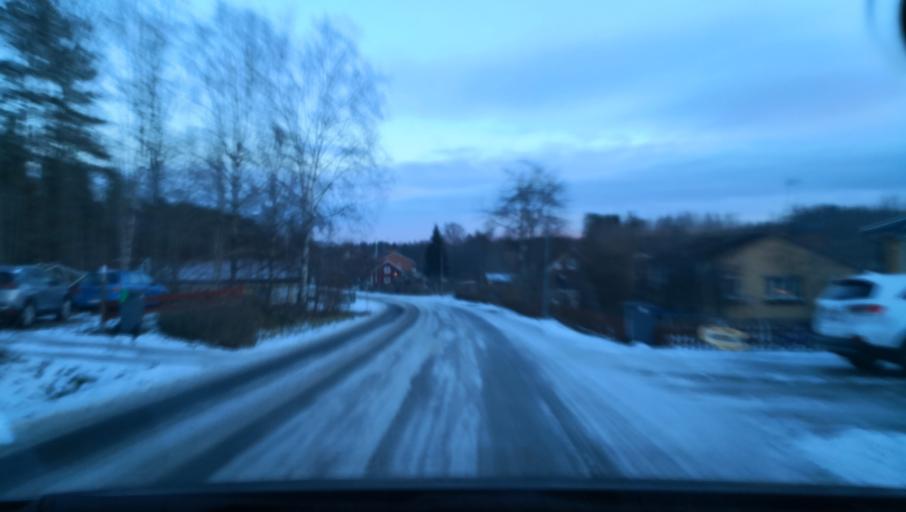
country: SE
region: Soedermanland
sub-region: Katrineholms Kommun
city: Katrineholm
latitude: 59.0908
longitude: 16.2048
